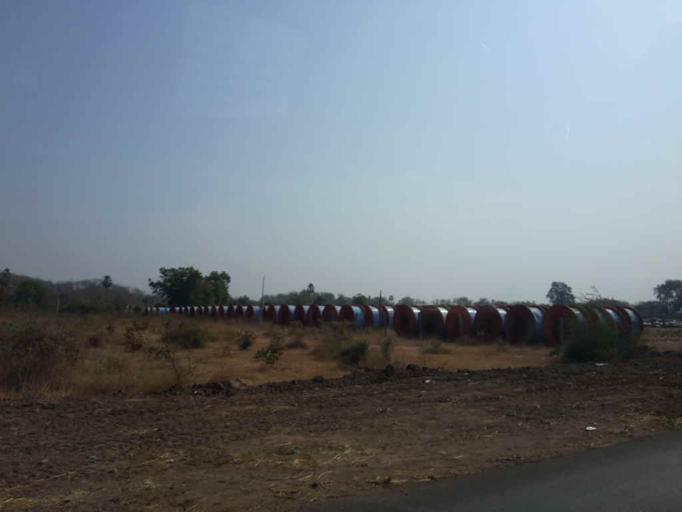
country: IN
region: Telangana
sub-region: Karimnagar
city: Koratla
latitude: 18.8475
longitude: 78.5940
